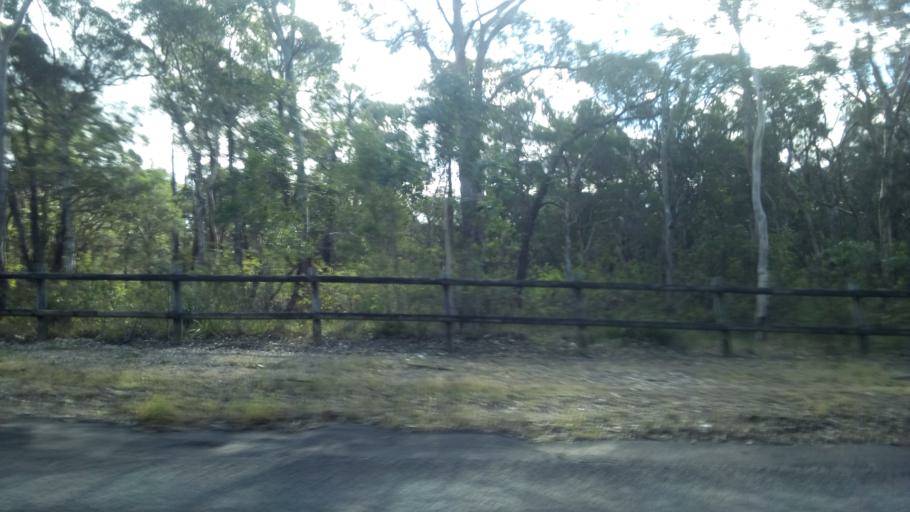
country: AU
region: New South Wales
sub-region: Shellharbour
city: Albion Park Rail
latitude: -34.5372
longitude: 150.7835
